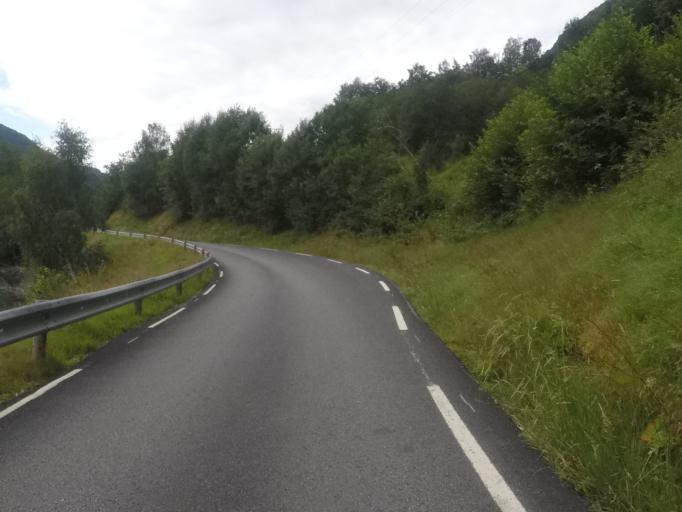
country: NO
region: Sogn og Fjordane
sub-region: Stryn
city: Stryn
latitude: 61.8462
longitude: 6.9328
